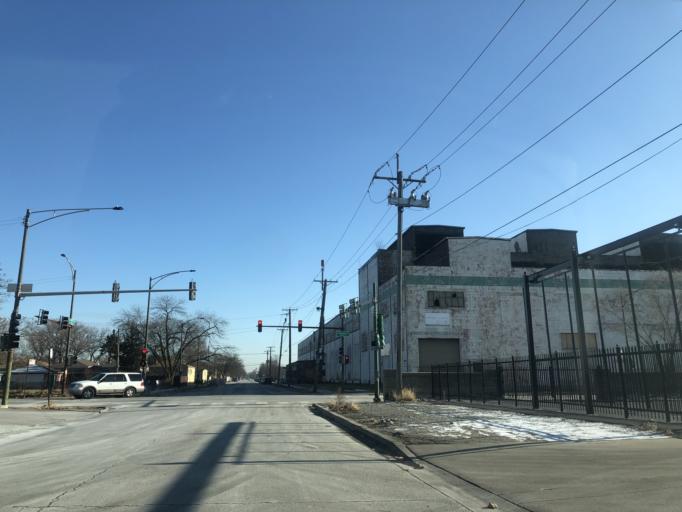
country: US
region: Illinois
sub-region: Cook County
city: Evergreen Park
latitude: 41.7594
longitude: -87.6739
